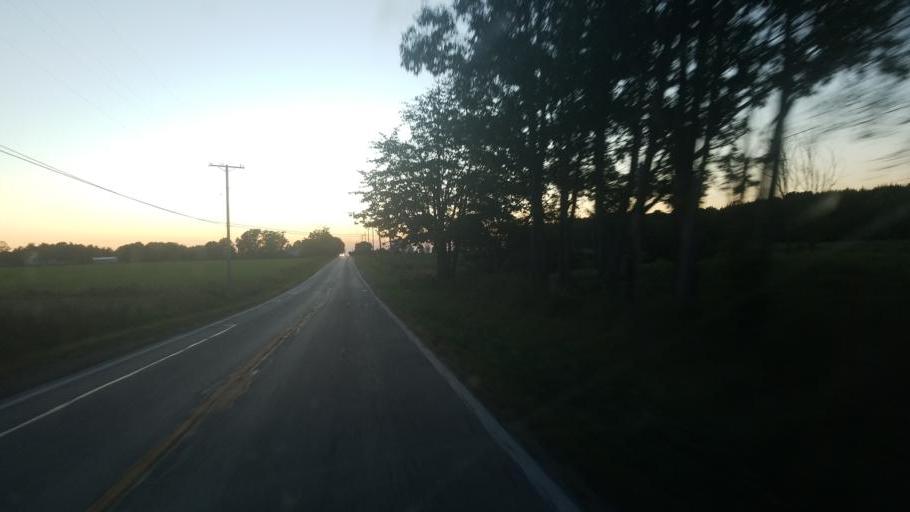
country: US
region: Ohio
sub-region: Ashtabula County
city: Jefferson
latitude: 41.7522
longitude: -80.6256
